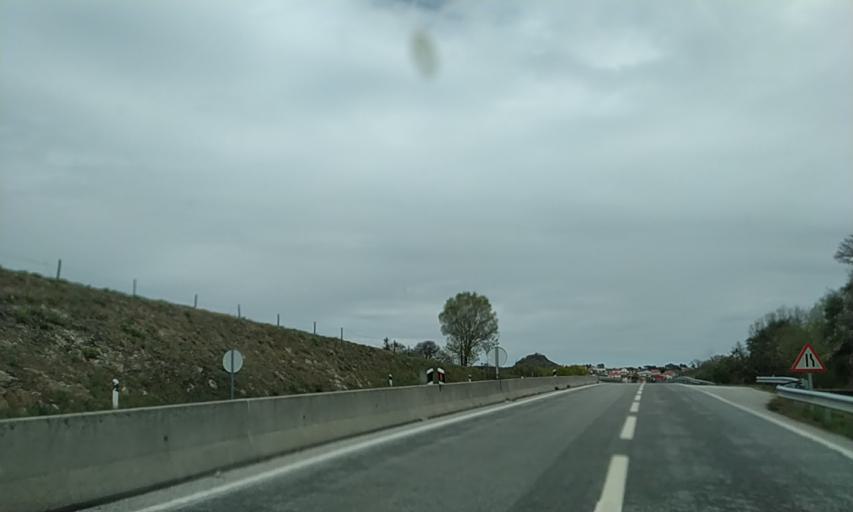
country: PT
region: Guarda
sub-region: Guarda
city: Guarda
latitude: 40.5868
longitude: -7.2719
